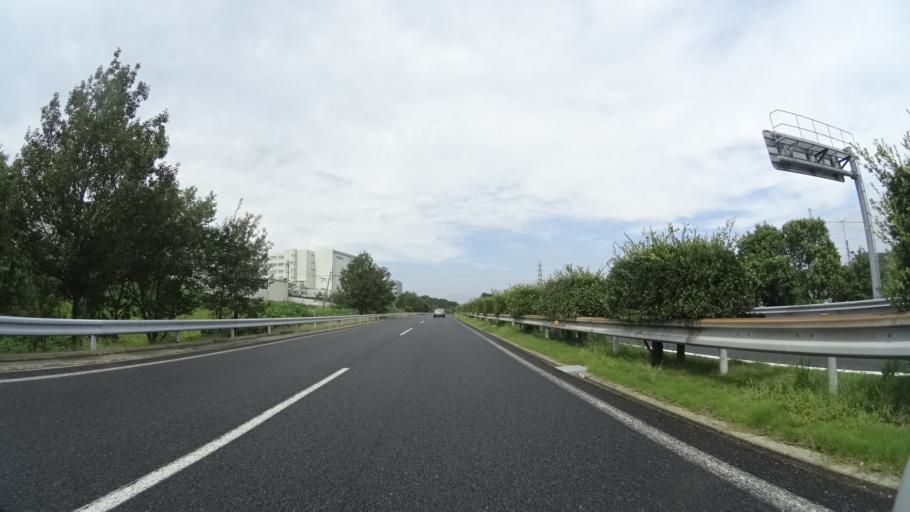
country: JP
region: Hyogo
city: Yashiro
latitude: 34.9299
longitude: 134.9383
